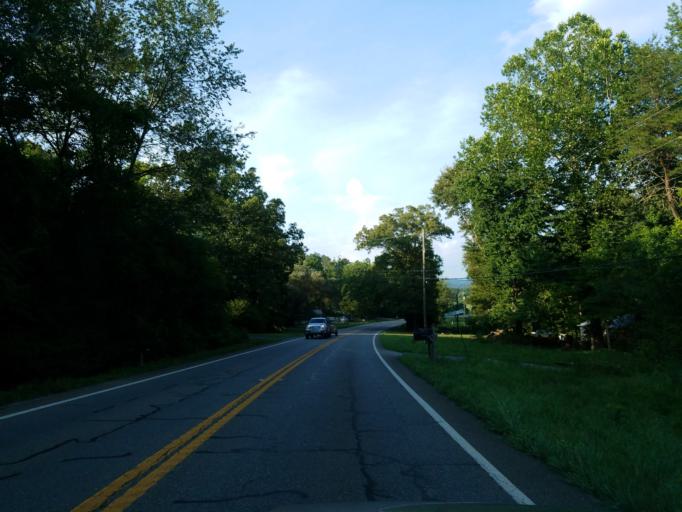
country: US
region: Georgia
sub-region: Pickens County
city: Jasper
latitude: 34.5138
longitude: -84.5442
